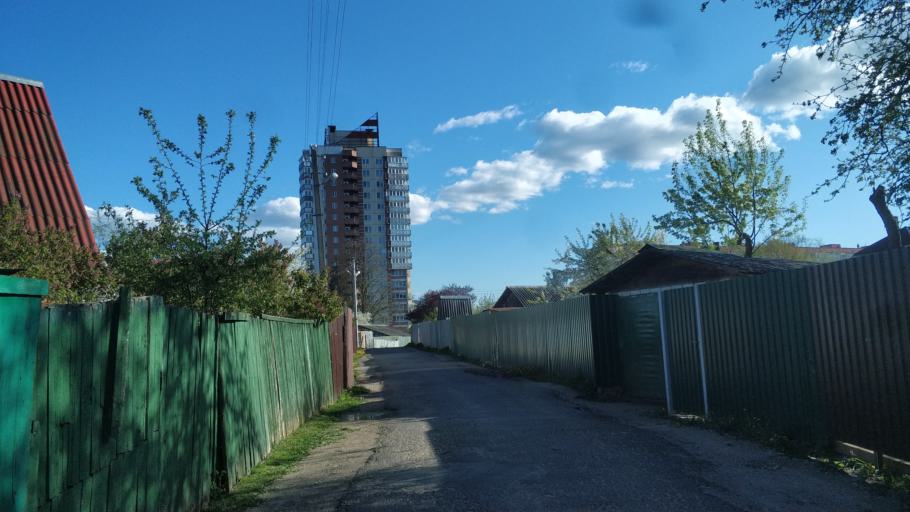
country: BY
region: Minsk
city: Minsk
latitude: 53.8726
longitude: 27.5804
